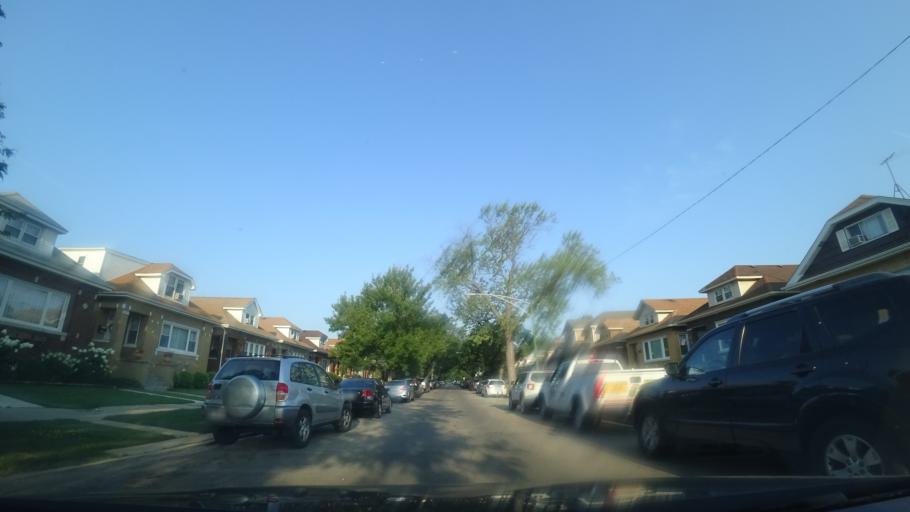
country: US
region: Illinois
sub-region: Cook County
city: Elmwood Park
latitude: 41.9404
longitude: -87.7674
